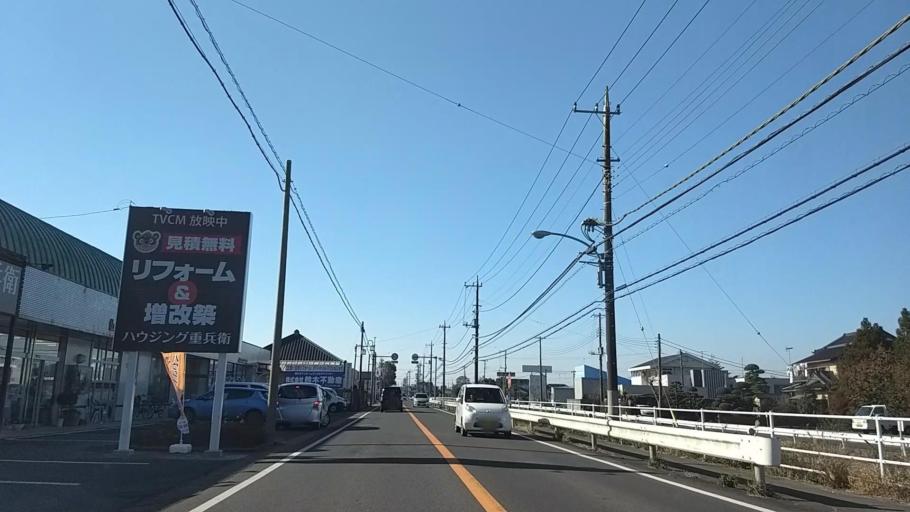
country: JP
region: Chiba
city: Asahi
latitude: 35.7213
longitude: 140.6121
